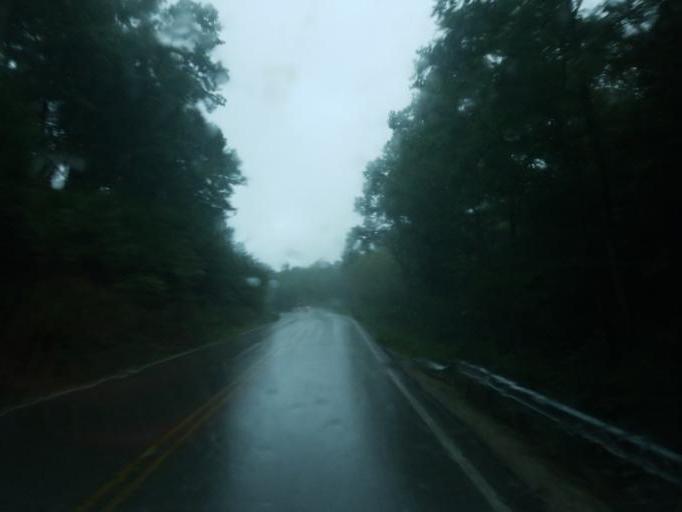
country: US
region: Kentucky
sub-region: Carter County
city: Olive Hill
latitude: 38.3374
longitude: -83.2019
